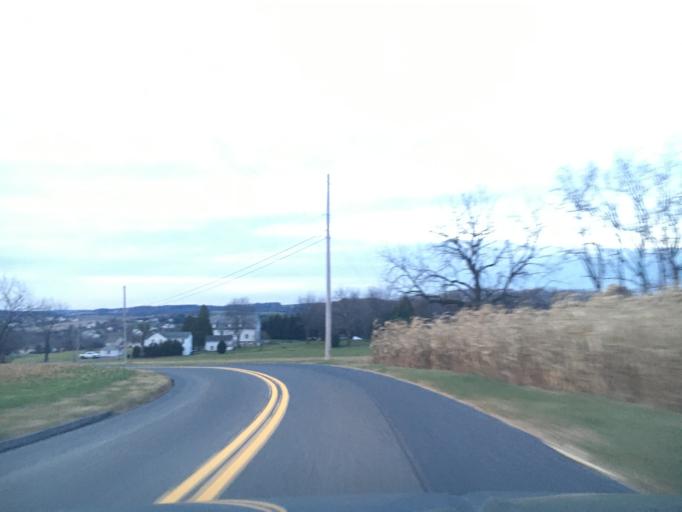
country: US
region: Pennsylvania
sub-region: Lehigh County
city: Schnecksville
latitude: 40.6923
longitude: -75.5766
